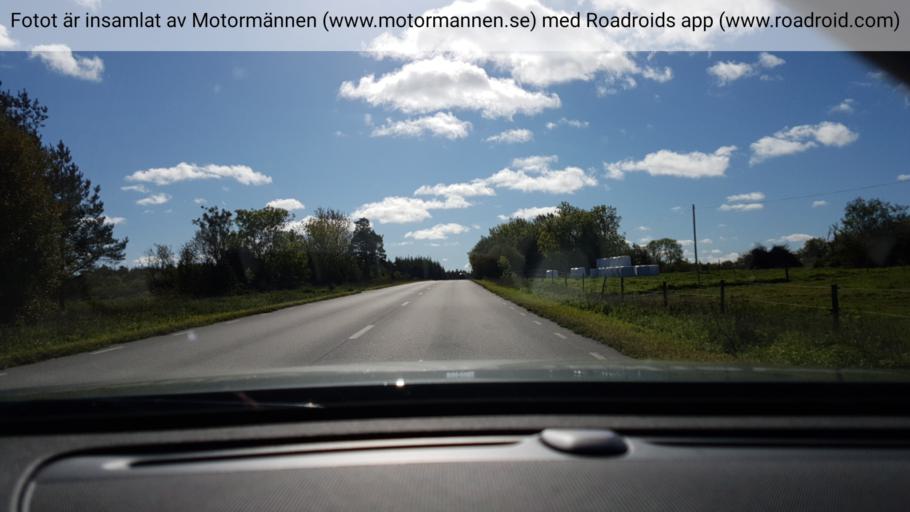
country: SE
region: Gotland
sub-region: Gotland
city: Slite
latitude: 57.7595
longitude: 18.7903
